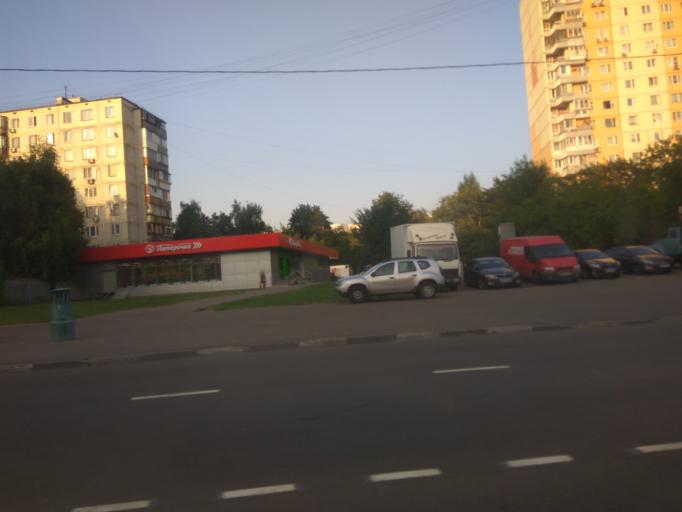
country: RU
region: Moscow
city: Orekhovo-Borisovo
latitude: 55.6059
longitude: 37.7124
